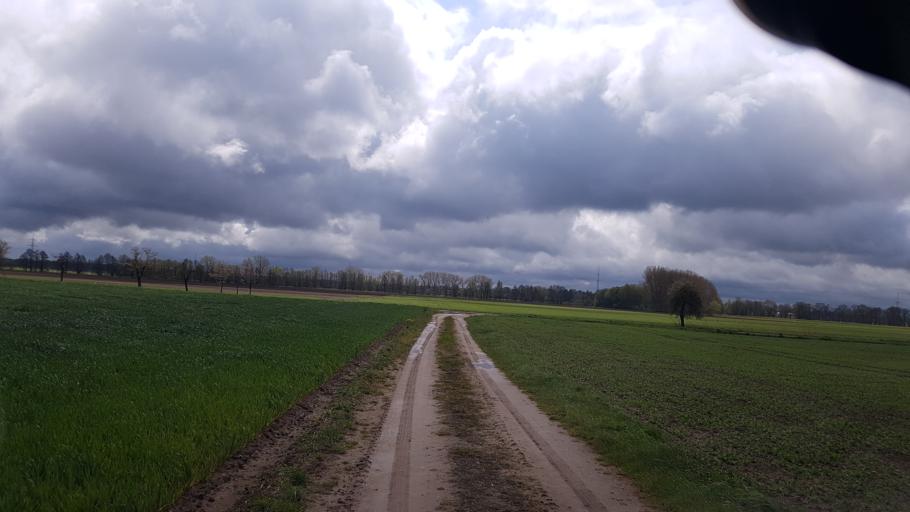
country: DE
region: Brandenburg
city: Doberlug-Kirchhain
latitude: 51.6555
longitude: 13.5542
